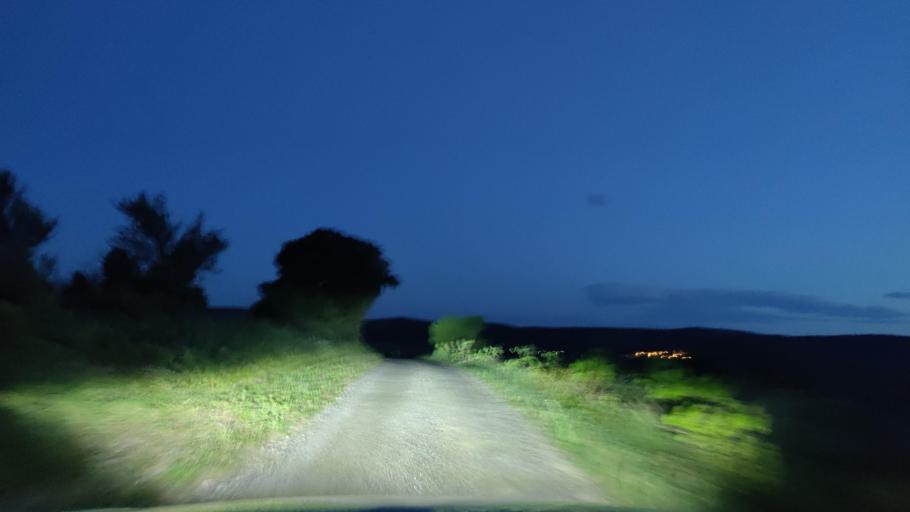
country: FR
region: Languedoc-Roussillon
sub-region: Departement des Pyrenees-Orientales
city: Estagel
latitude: 42.8725
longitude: 2.7292
